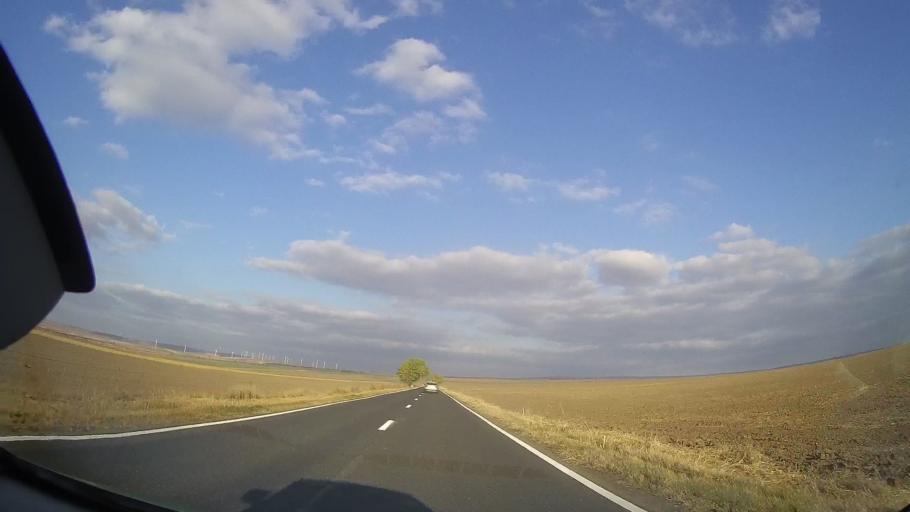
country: RO
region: Tulcea
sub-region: Comuna Topolog
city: Topolog
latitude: 44.8356
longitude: 28.2940
